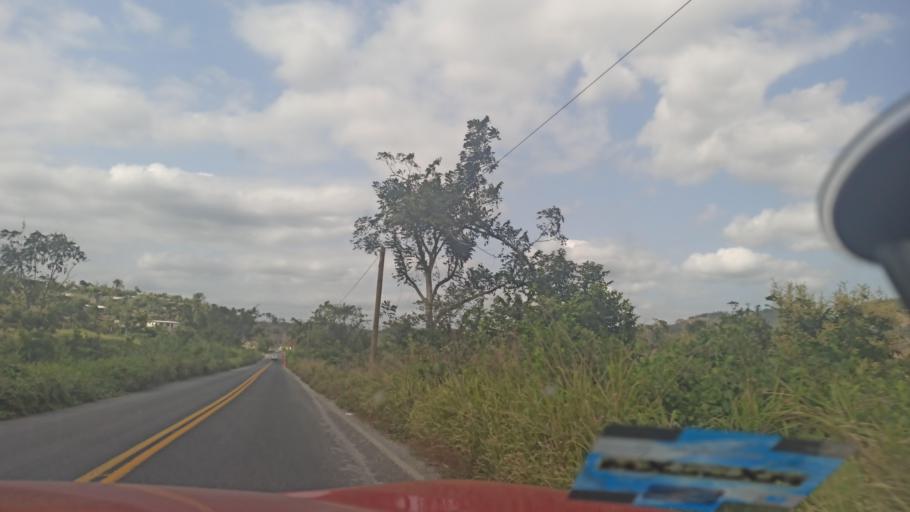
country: MX
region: Veracruz
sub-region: Papantla
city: Polutla
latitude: 20.4623
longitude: -97.2530
